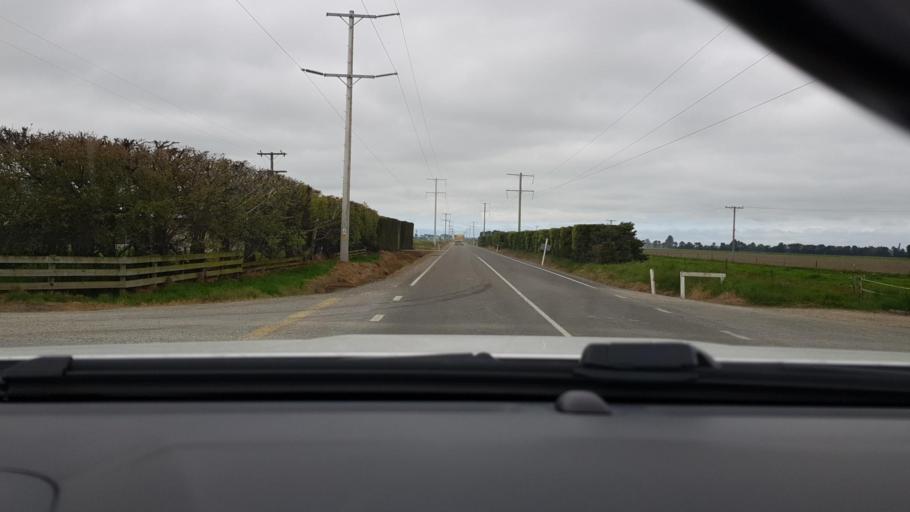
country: NZ
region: Otago
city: Oamaru
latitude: -44.9647
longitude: 170.9775
